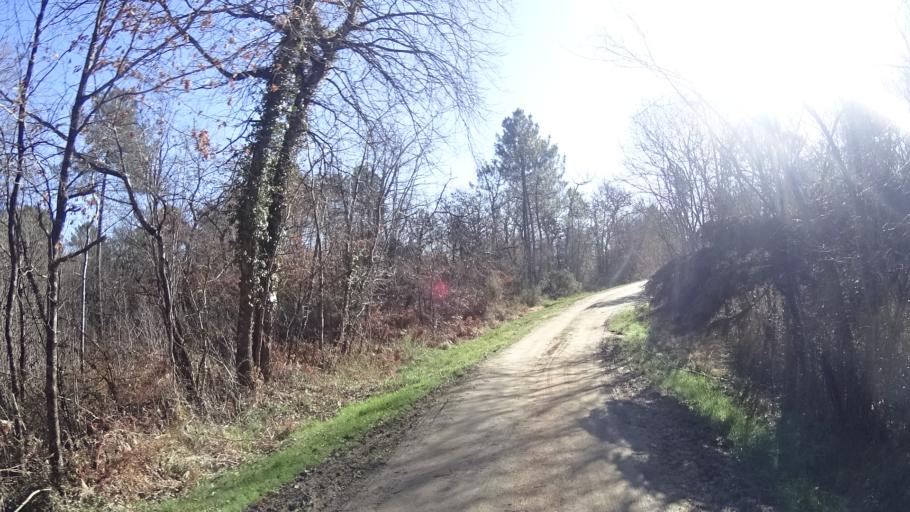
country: FR
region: Poitou-Charentes
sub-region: Departement de la Charente
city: Chalais
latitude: 45.2107
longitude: 0.0647
